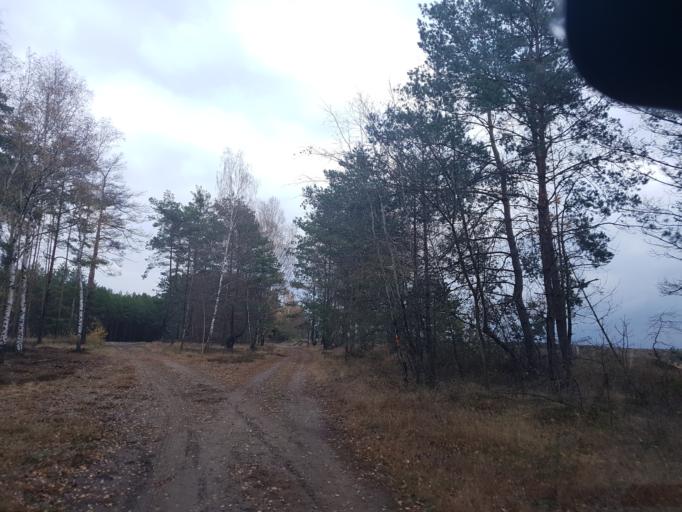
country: DE
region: Brandenburg
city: Finsterwalde
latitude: 51.6398
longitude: 13.6667
